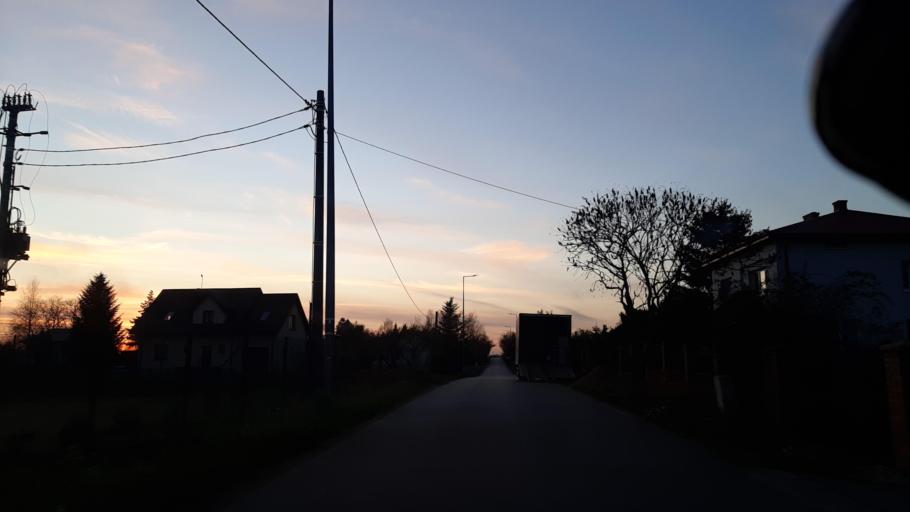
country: PL
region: Lublin Voivodeship
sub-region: Powiat lubelski
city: Jastkow
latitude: 51.3241
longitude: 22.4404
